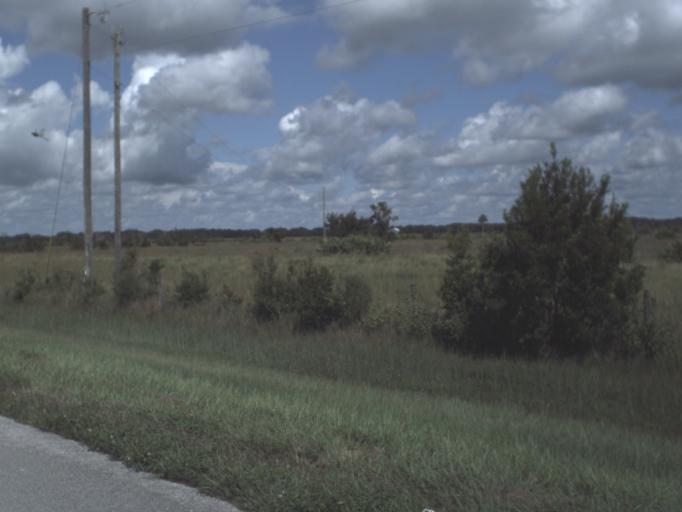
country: US
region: Florida
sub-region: Highlands County
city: Lake Placid
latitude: 27.4059
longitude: -81.1758
